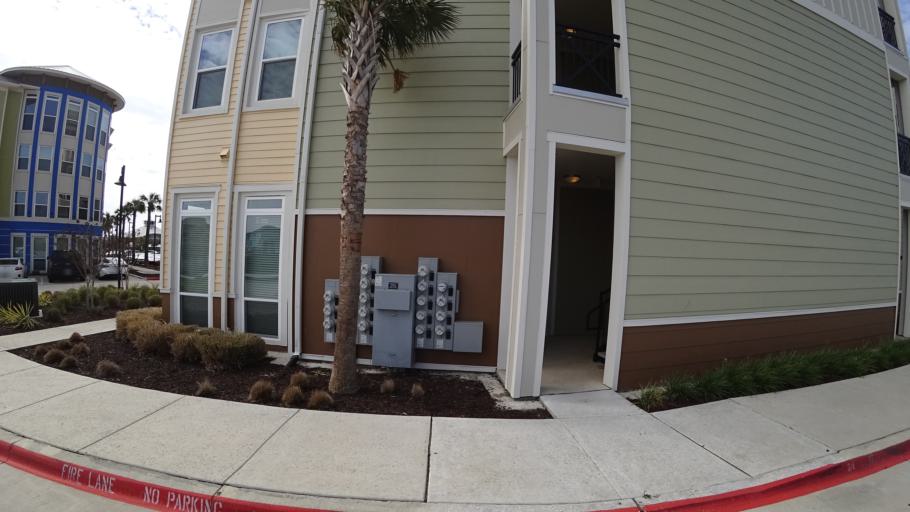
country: US
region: Texas
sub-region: Denton County
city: Lewisville
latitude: 33.0076
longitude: -96.9582
